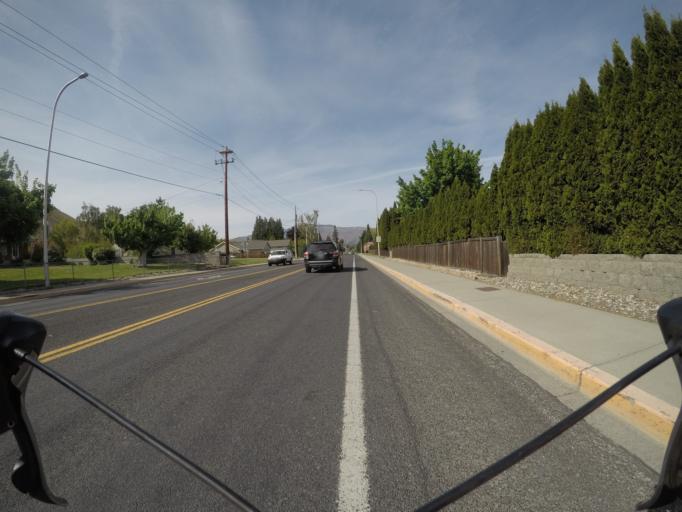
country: US
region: Washington
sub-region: Chelan County
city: West Wenatchee
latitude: 47.4159
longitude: -120.3461
